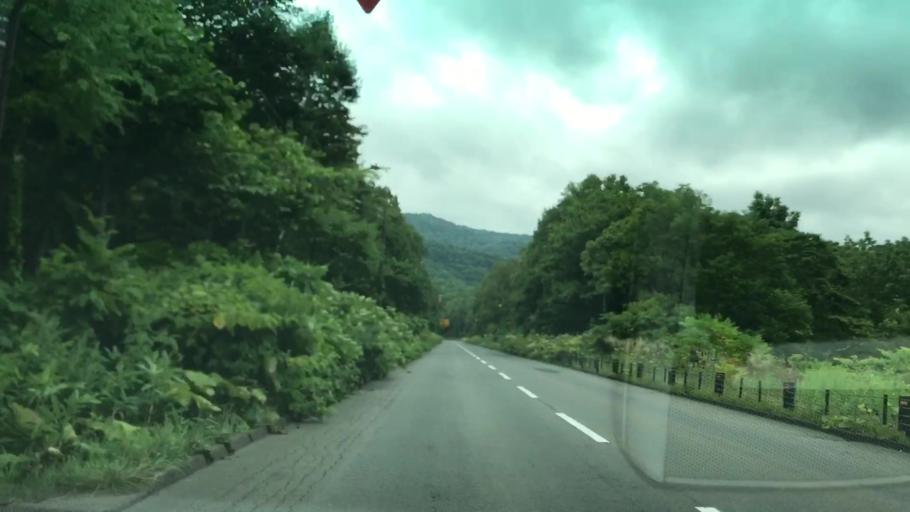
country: JP
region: Hokkaido
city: Yoichi
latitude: 43.0092
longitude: 140.8724
